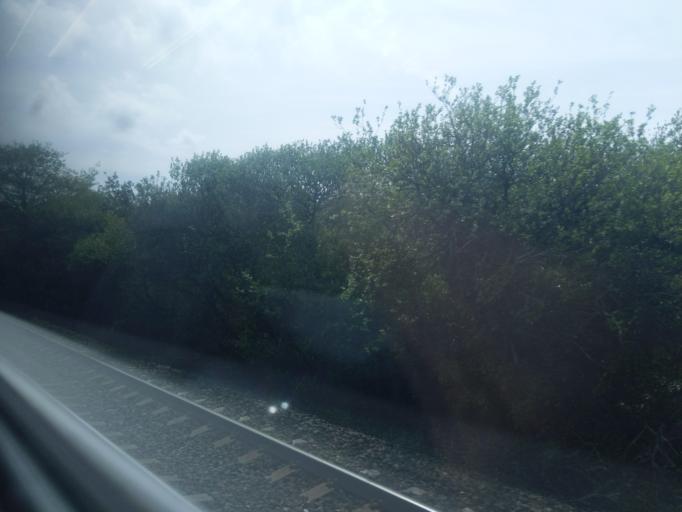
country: GB
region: England
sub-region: Cornwall
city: Marazion
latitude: 50.1439
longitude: -5.4663
